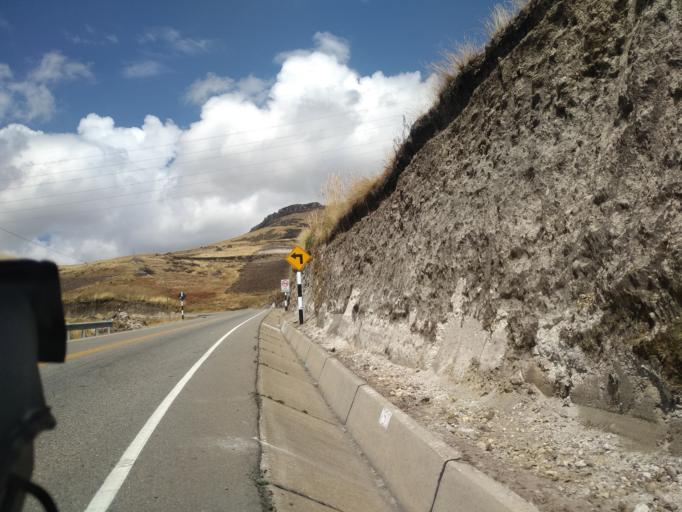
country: PE
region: La Libertad
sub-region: Provincia de Santiago de Chuco
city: Quiruvilca
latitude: -7.9214
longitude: -78.1522
